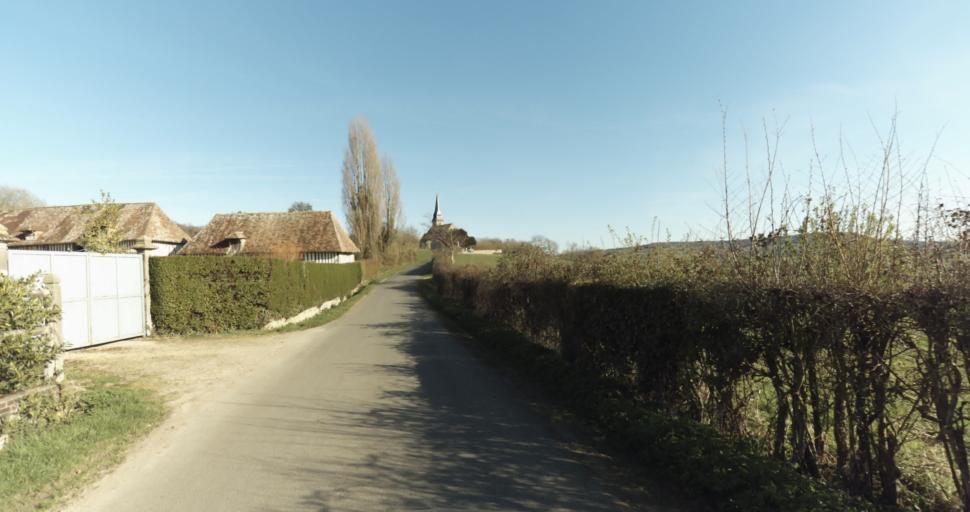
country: FR
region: Lower Normandy
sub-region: Departement du Calvados
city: Saint-Pierre-sur-Dives
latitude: 49.0409
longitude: 0.0361
